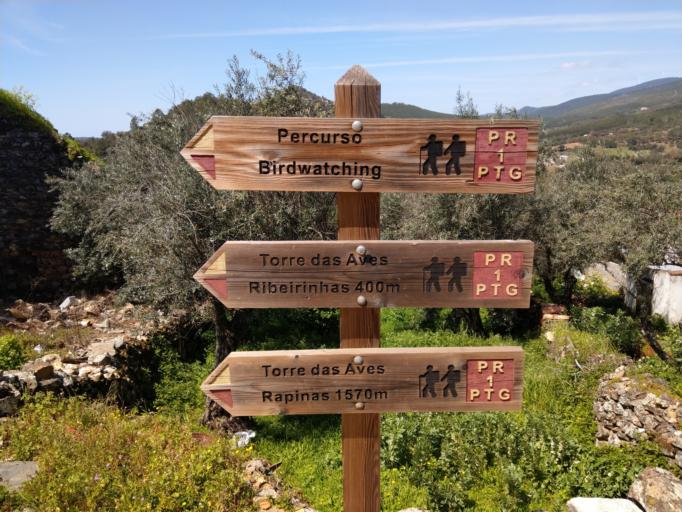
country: PT
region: Portalegre
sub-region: Portalegre
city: Alegrete
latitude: 39.2373
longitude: -7.3245
